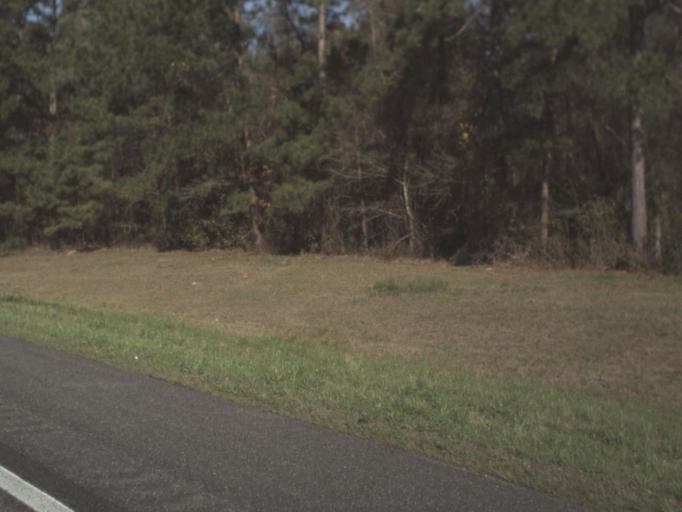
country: US
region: Florida
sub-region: Jefferson County
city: Monticello
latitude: 30.4786
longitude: -83.9146
